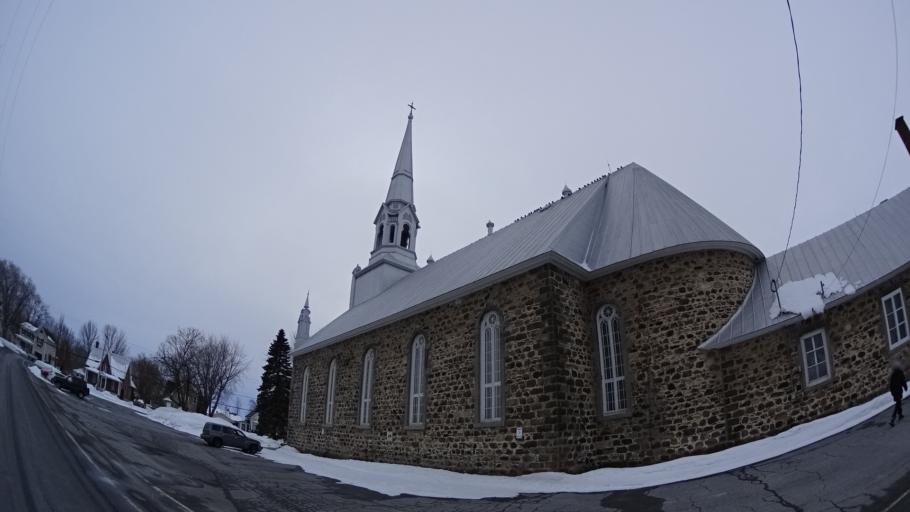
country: CA
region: Quebec
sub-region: Monteregie
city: Bedford
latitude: 45.1713
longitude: -73.0306
